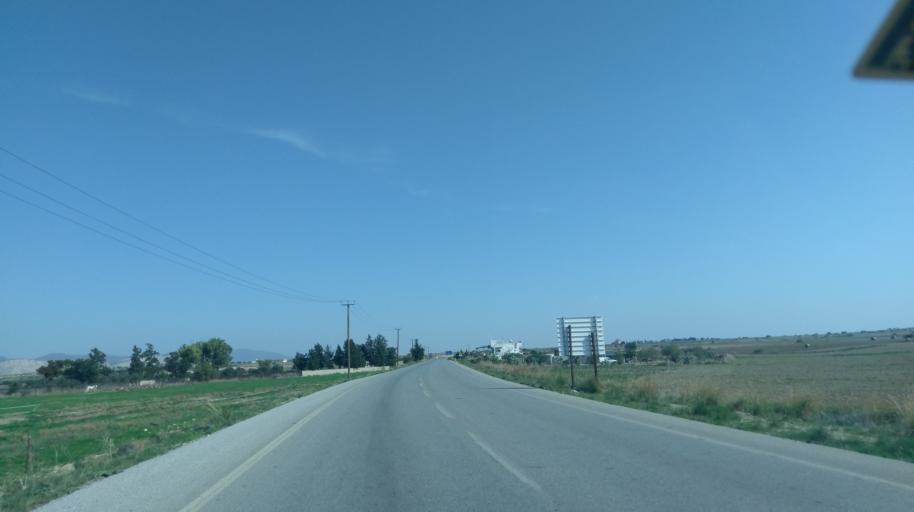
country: CY
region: Ammochostos
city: Lefkonoiko
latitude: 35.2586
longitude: 33.7385
